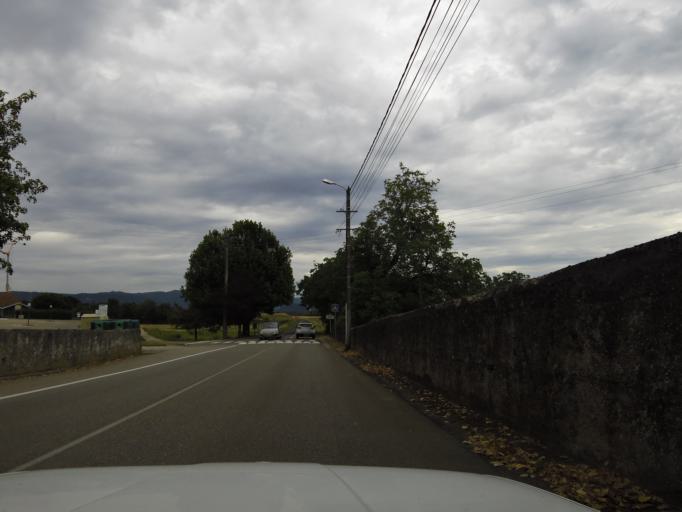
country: FR
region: Rhone-Alpes
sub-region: Departement de l'Ain
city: Chazey-sur-Ain
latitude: 45.8921
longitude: 5.2574
